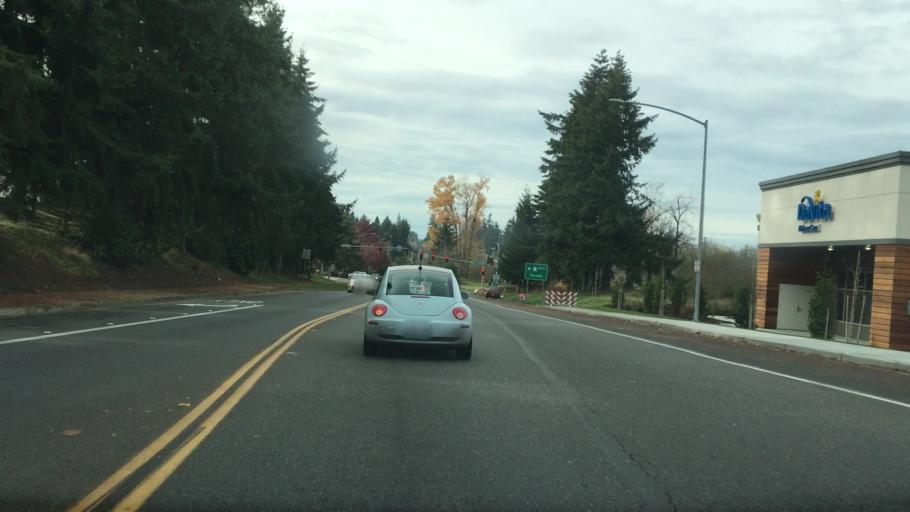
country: US
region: Washington
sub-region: Pierce County
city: Puyallup
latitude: 47.1623
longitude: -122.3020
